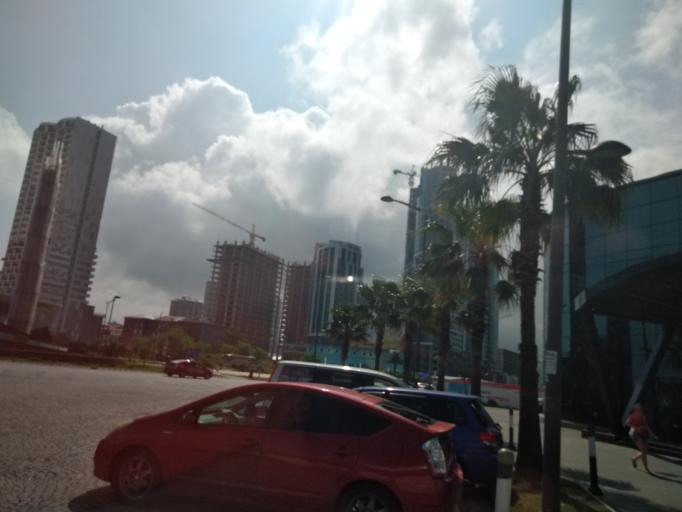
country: GE
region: Ajaria
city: Batumi
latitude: 41.6404
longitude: 41.6139
